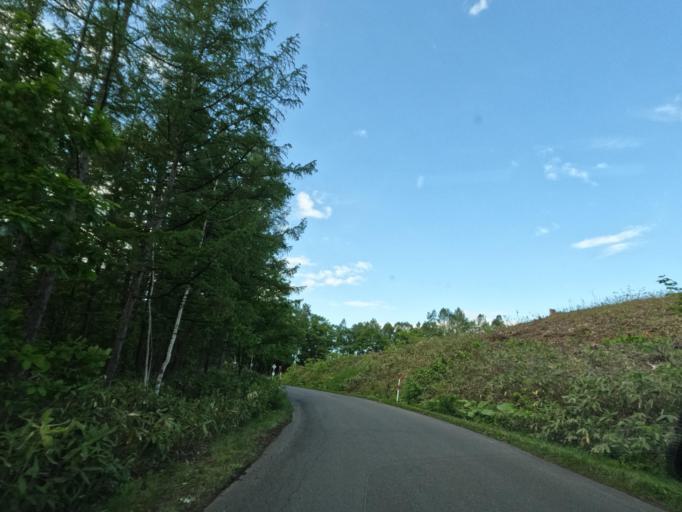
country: JP
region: Hokkaido
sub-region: Asahikawa-shi
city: Asahikawa
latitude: 43.8788
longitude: 142.4545
